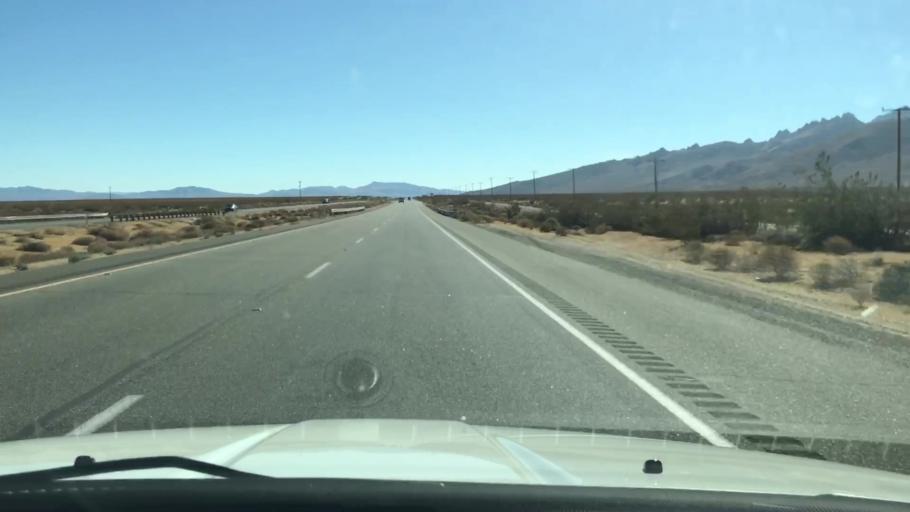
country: US
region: California
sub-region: Kern County
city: Inyokern
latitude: 35.7588
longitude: -117.8709
